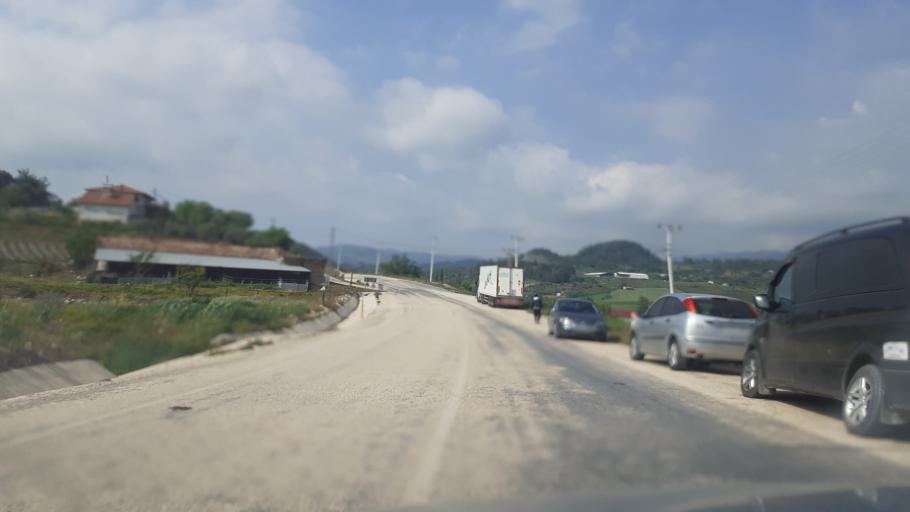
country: TR
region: Hatay
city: Yayladagi
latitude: 35.9097
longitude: 36.0539
